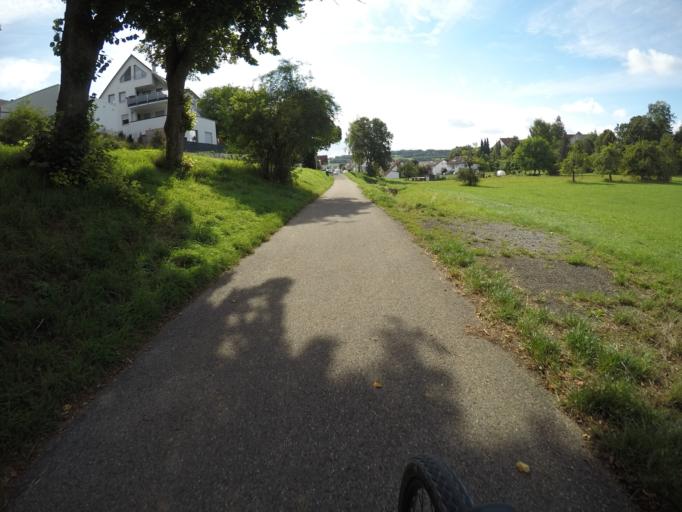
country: DE
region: Baden-Wuerttemberg
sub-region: Karlsruhe Region
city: Gechingen
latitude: 48.6988
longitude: 8.8246
